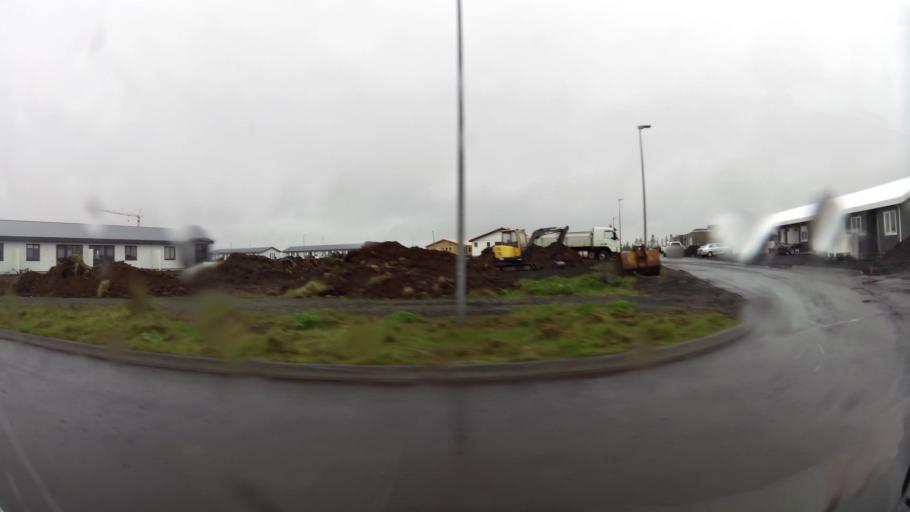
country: IS
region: South
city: Selfoss
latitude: 63.9296
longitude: -21.0288
